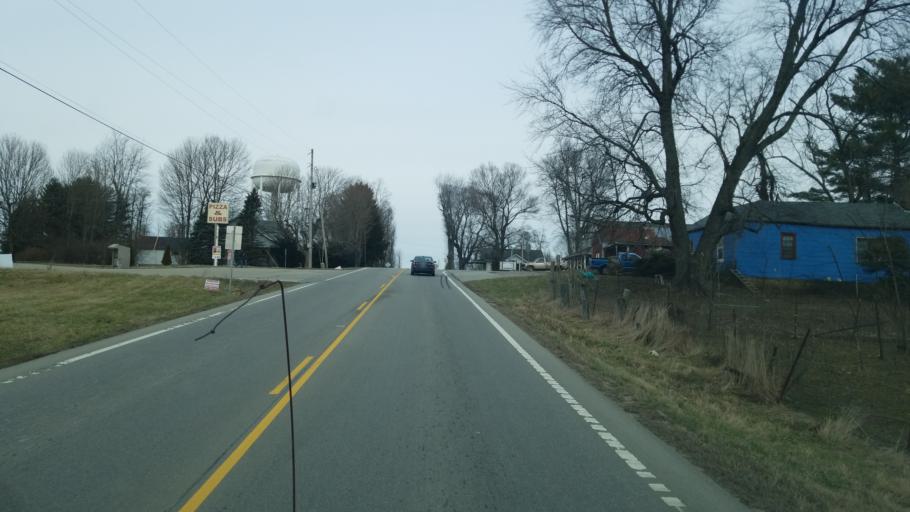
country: US
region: Ohio
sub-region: Highland County
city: Hillsboro
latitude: 39.1348
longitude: -83.6688
